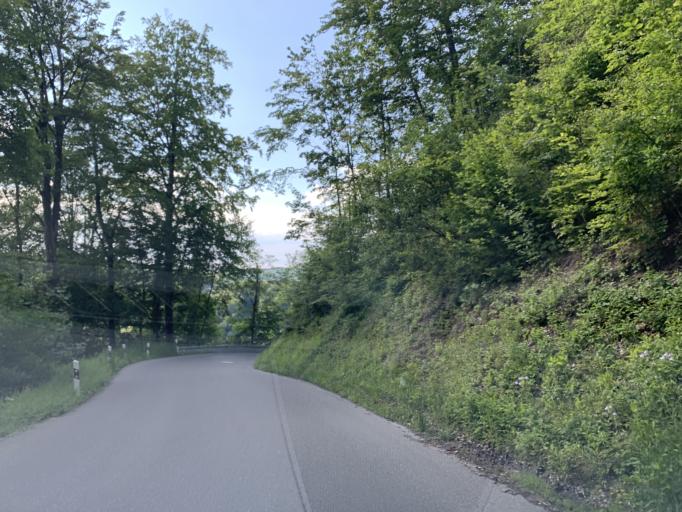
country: CH
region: Zurich
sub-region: Bezirk Winterthur
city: Seen (Kreis 3) / Waldegg
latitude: 47.4583
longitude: 8.7426
